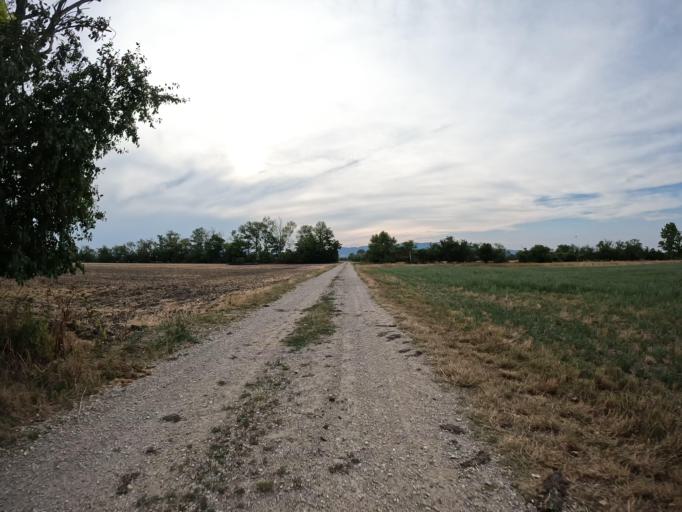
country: AT
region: Lower Austria
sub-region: Politischer Bezirk Baden
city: Trumau
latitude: 48.0035
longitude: 16.3351
